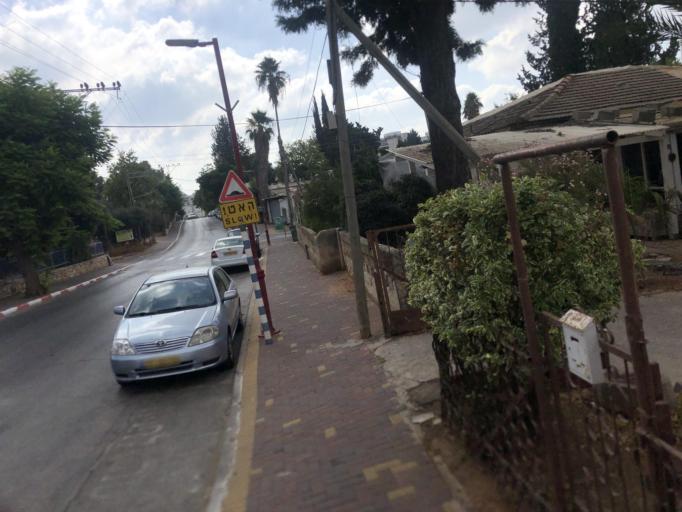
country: IL
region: Central District
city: Yehud
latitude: 32.0340
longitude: 34.8868
